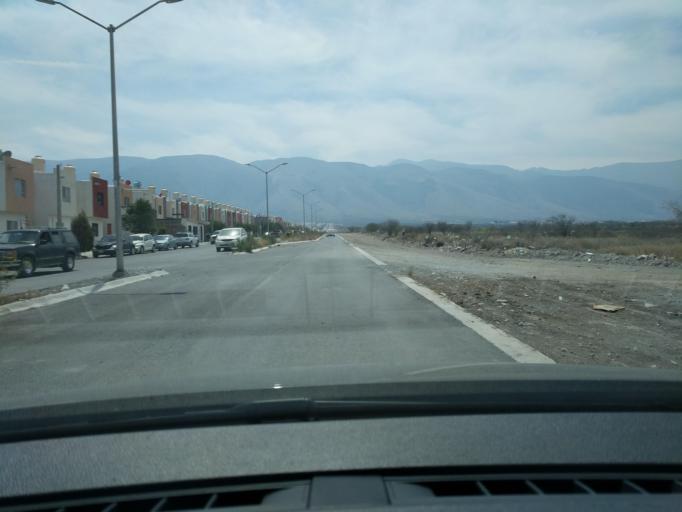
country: MX
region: Coahuila
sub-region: Arteaga
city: Arteaga
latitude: 25.4256
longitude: -100.9127
